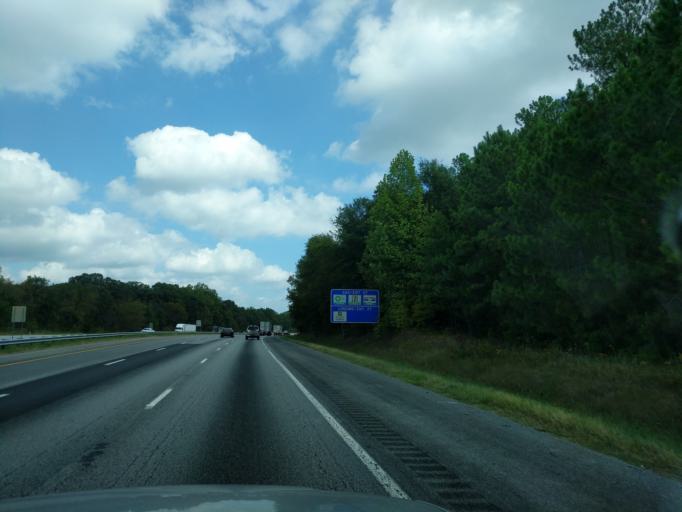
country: US
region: South Carolina
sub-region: Anderson County
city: Northlake
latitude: 34.6259
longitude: -82.6118
